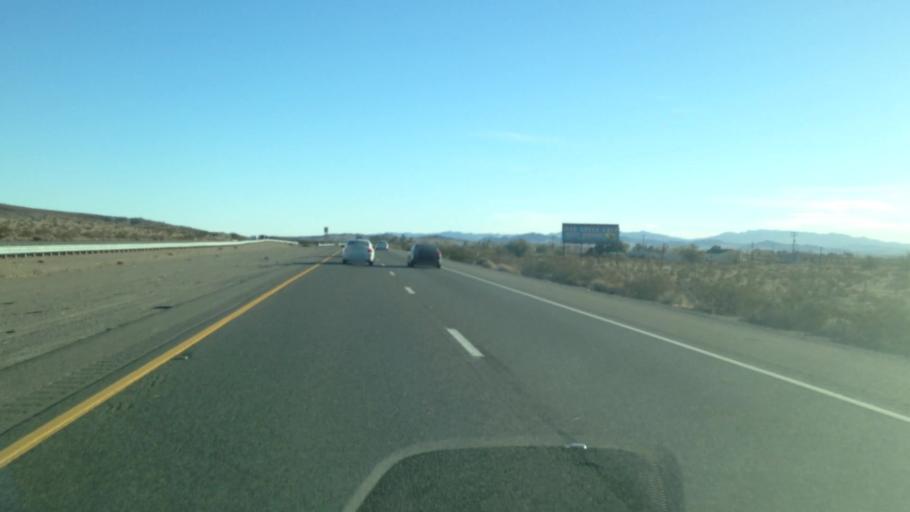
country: US
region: California
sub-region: San Bernardino County
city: Barstow
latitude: 34.9266
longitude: -116.7296
